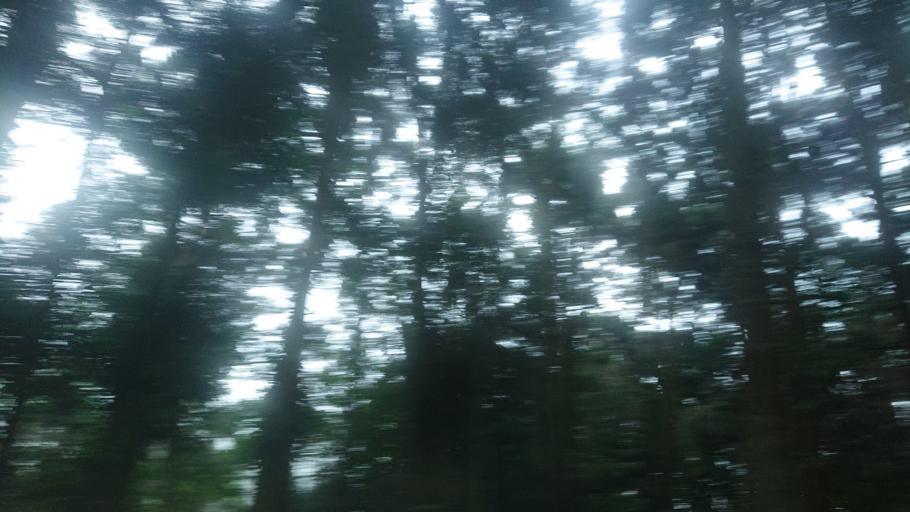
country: TW
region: Taiwan
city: Lugu
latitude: 23.6231
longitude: 120.7187
